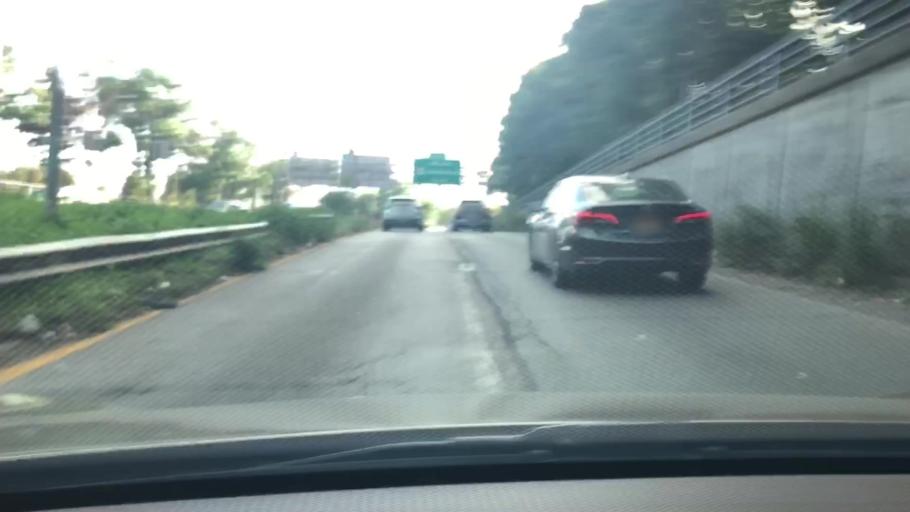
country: US
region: New York
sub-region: Queens County
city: Long Island City
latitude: 40.7658
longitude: -73.8945
